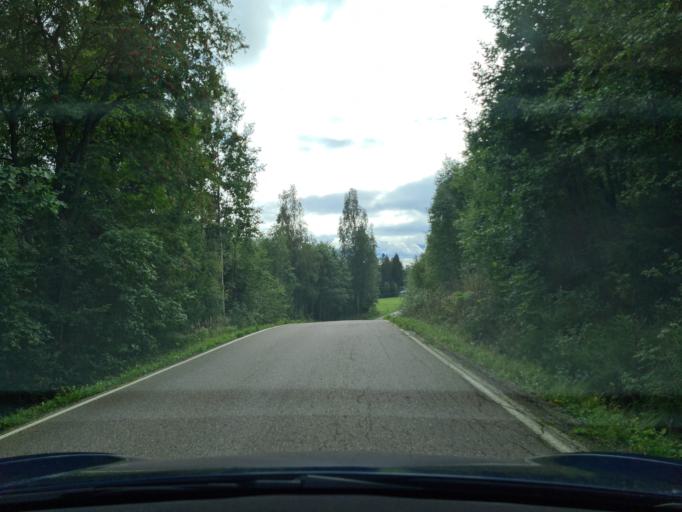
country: FI
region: Uusimaa
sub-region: Helsinki
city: Vihti
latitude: 60.4629
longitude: 24.4334
